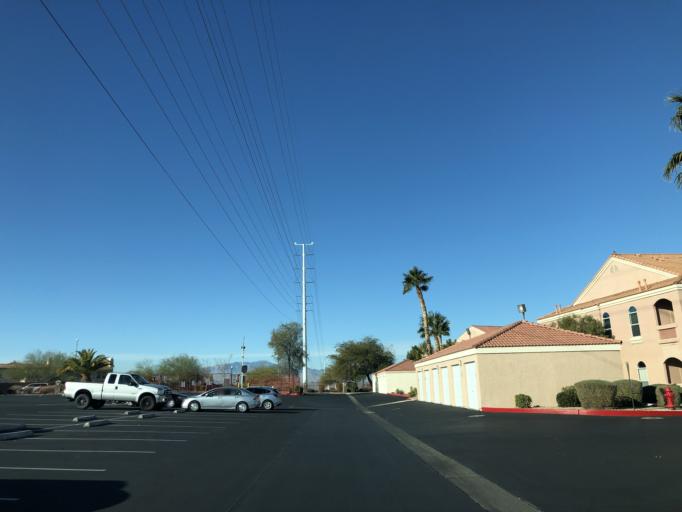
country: US
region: Nevada
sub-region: Clark County
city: Whitney
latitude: 36.0025
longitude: -115.0935
